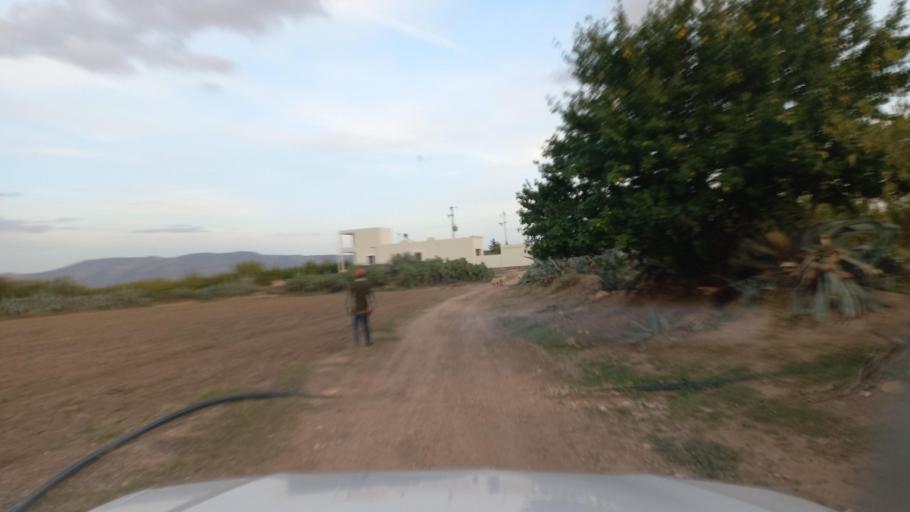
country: TN
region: Al Qasrayn
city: Sbiba
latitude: 35.4130
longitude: 9.1017
